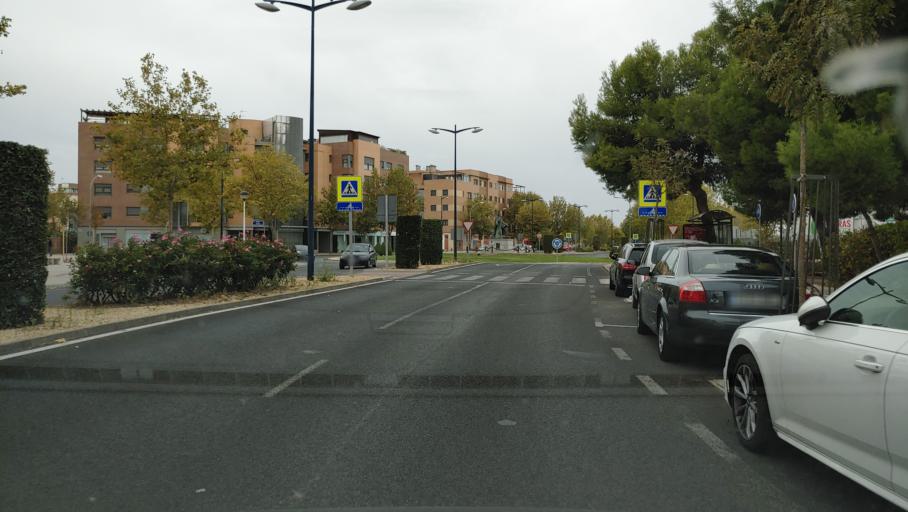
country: ES
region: Castille-La Mancha
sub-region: Provincia de Ciudad Real
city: Ciudad Real
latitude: 38.9727
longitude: -3.9348
